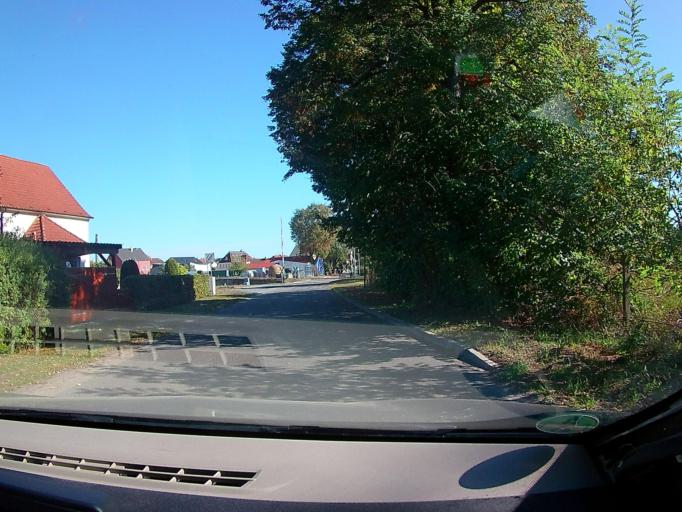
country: DE
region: Mecklenburg-Vorpommern
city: Wesenberg
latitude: 53.2859
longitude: 12.9604
